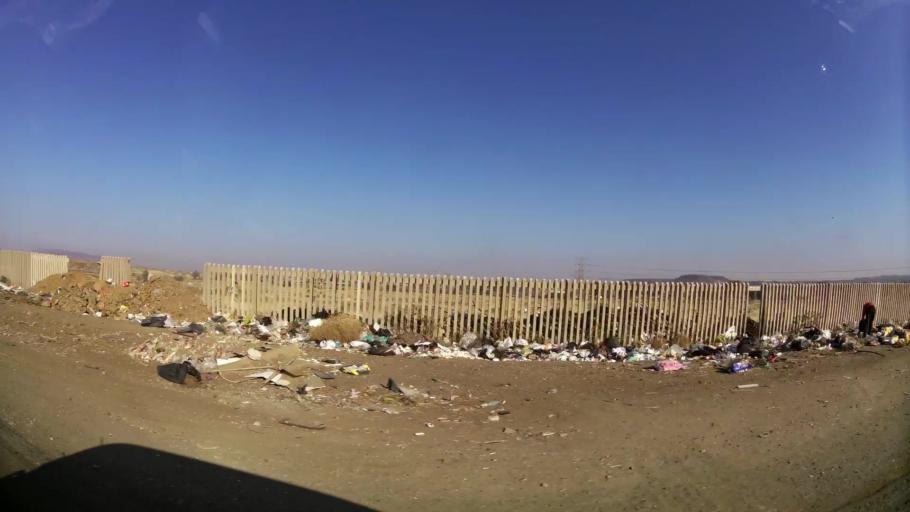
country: ZA
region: Orange Free State
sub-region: Mangaung Metropolitan Municipality
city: Bloemfontein
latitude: -29.1766
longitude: 26.1960
